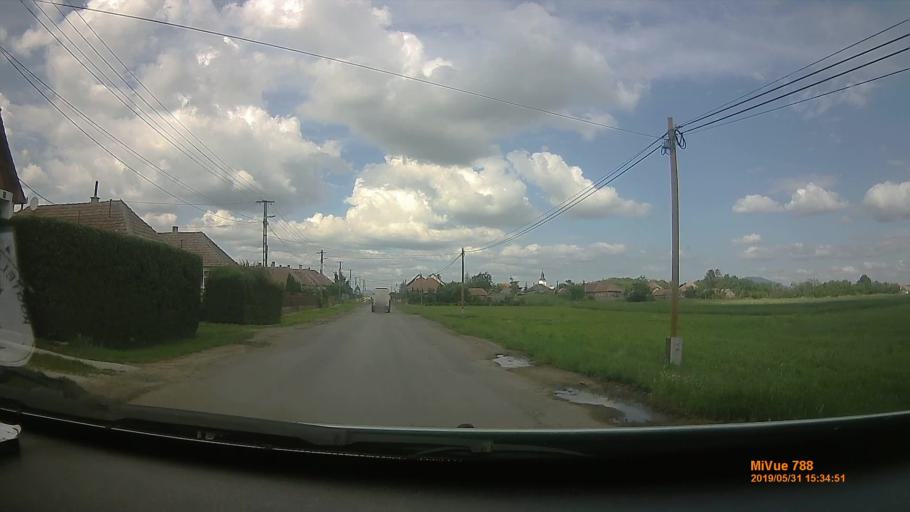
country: HU
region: Borsod-Abauj-Zemplen
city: Prugy
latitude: 48.0778
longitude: 21.2445
